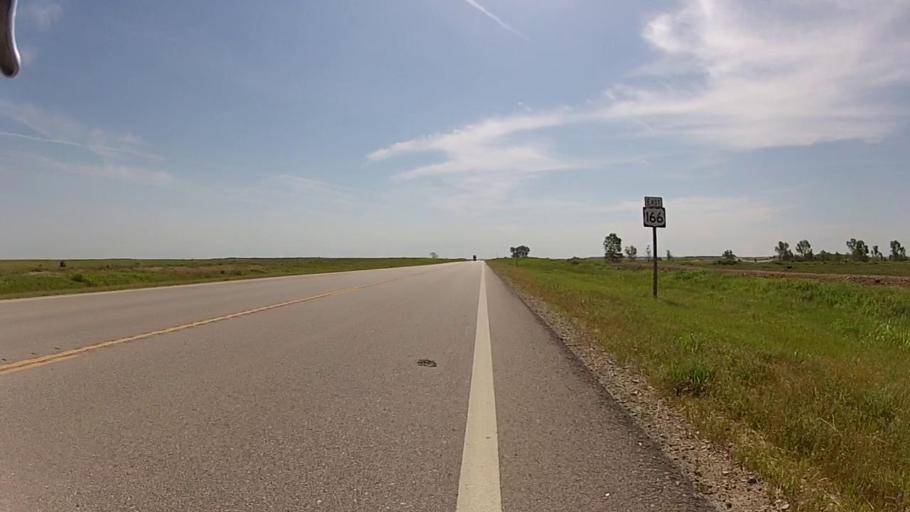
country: US
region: Kansas
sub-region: Cowley County
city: Winfield
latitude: 37.1110
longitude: -96.6172
